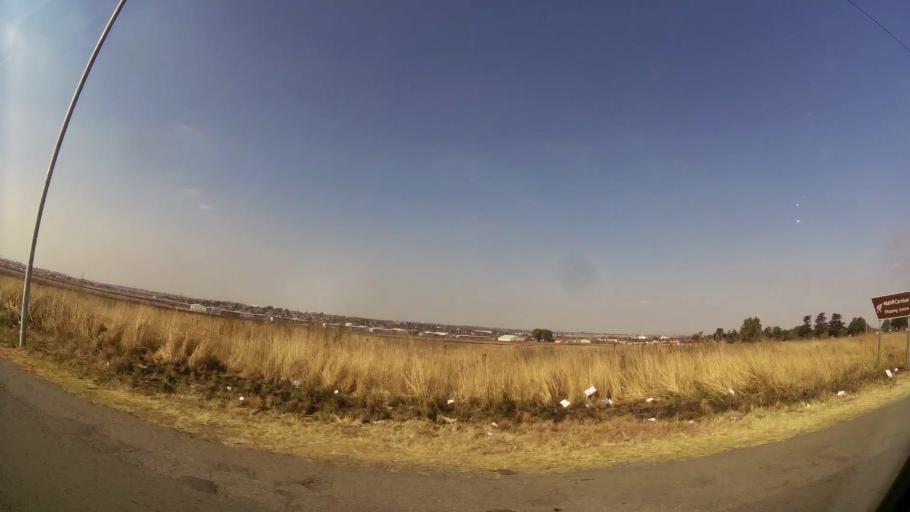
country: ZA
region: Gauteng
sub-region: Ekurhuleni Metropolitan Municipality
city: Boksburg
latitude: -26.2402
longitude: 28.2944
